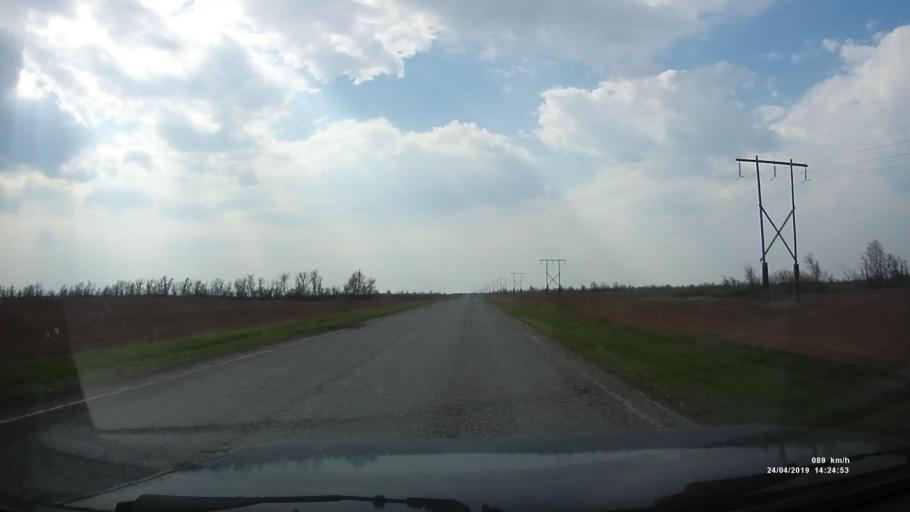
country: RU
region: Kalmykiya
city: Arshan'
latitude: 46.3293
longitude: 44.0890
